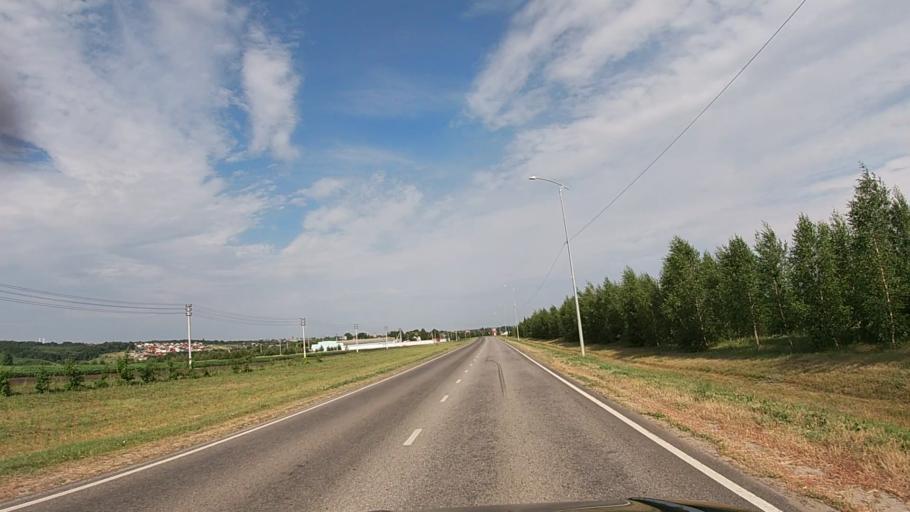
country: RU
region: Belgorod
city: Krasnaya Yaruga
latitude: 50.7976
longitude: 35.6852
